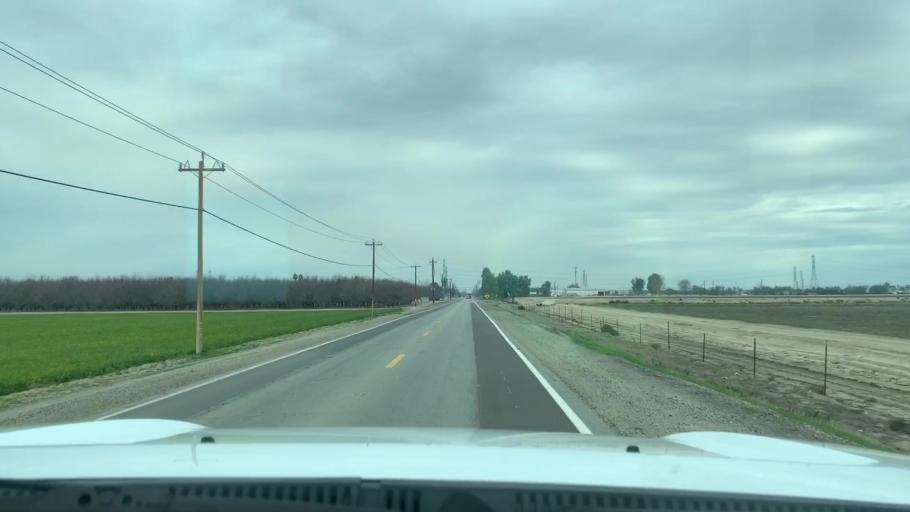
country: US
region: California
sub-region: Kern County
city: Rosedale
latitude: 35.3784
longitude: -119.2521
